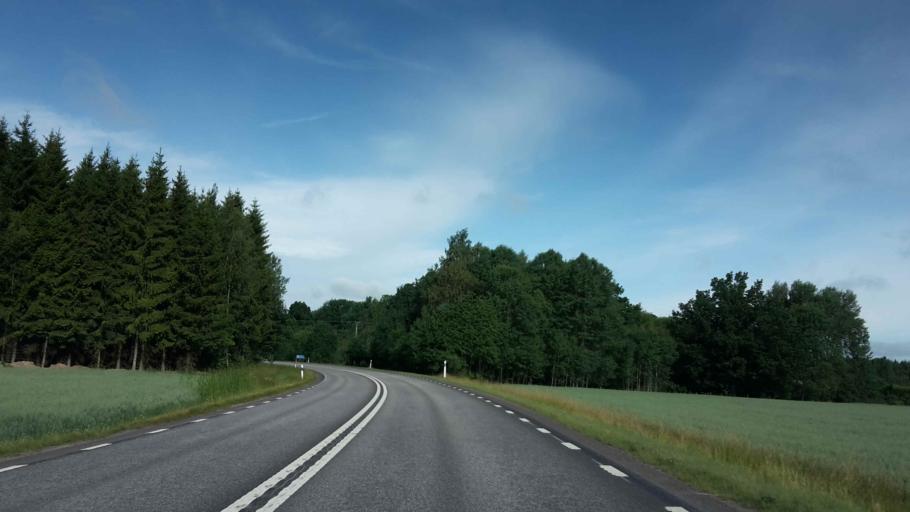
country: SE
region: OEstergoetland
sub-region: Motala Kommun
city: Borensberg
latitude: 58.5367
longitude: 15.3817
